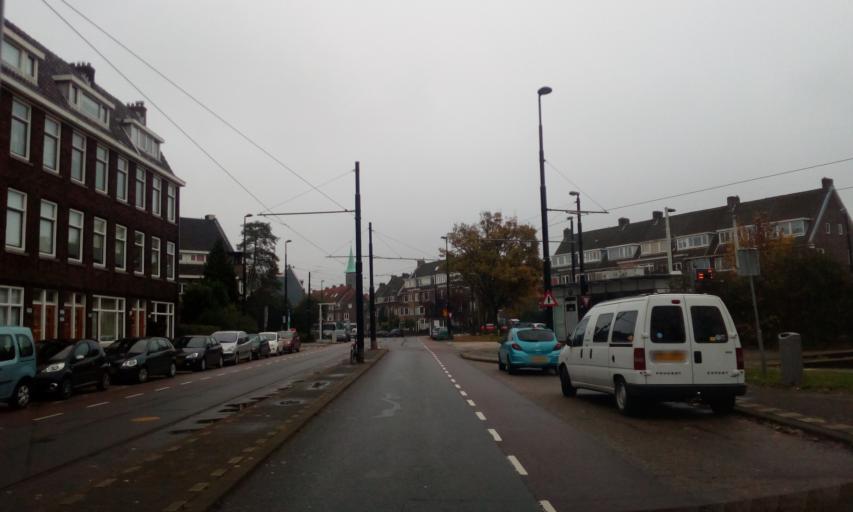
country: NL
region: South Holland
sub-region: Gemeente Rotterdam
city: Rotterdam
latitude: 51.9451
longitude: 4.4679
